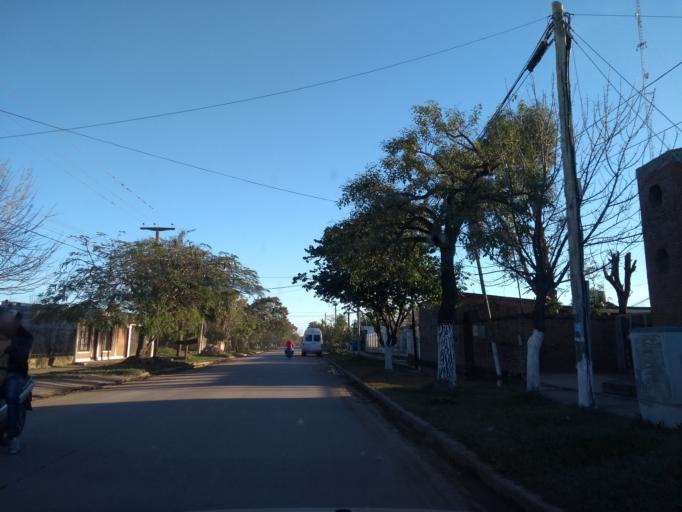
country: AR
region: Chaco
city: Barranqueras
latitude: -27.4959
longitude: -58.9559
